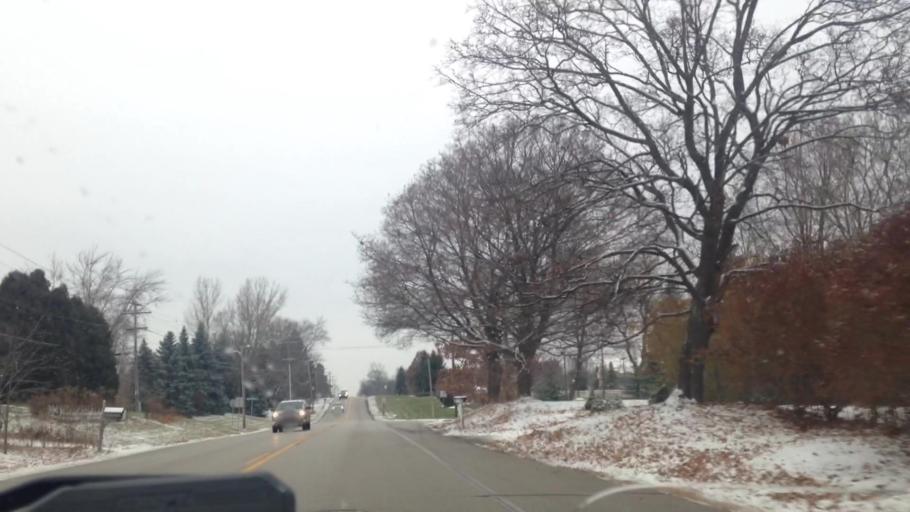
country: US
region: Wisconsin
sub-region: Waukesha County
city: Brookfield
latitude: 43.0960
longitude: -88.1057
